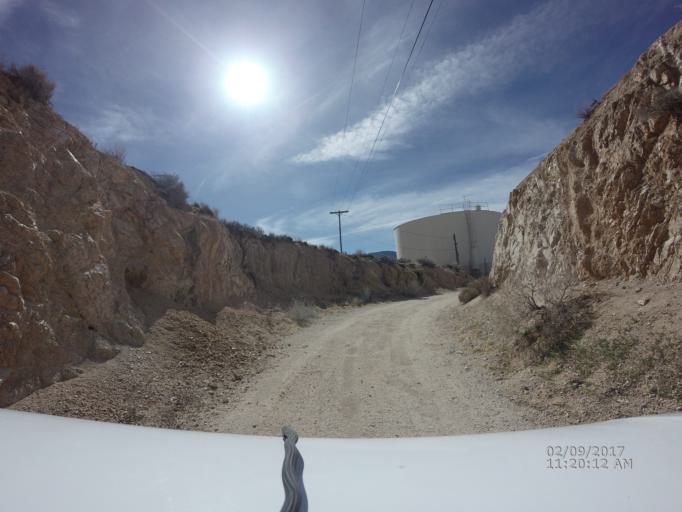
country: US
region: California
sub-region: Los Angeles County
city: Littlerock
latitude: 34.5001
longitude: -117.9229
